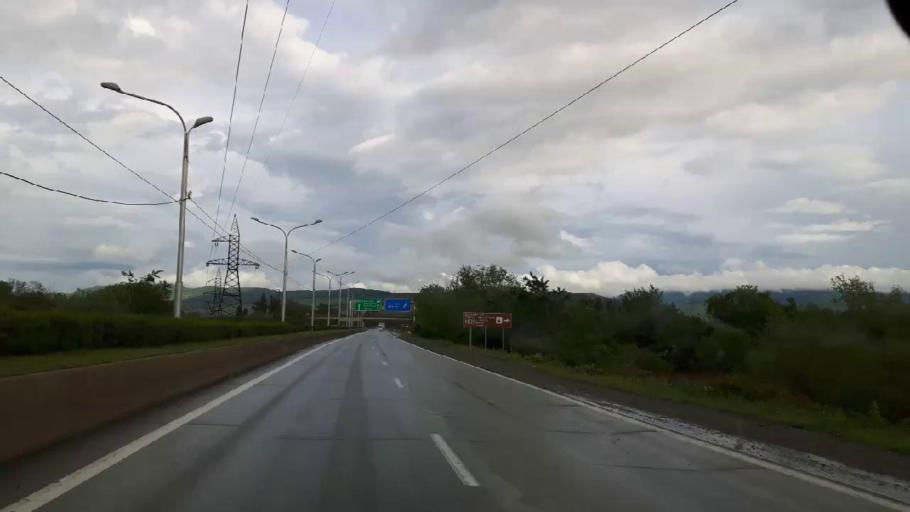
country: GE
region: Shida Kartli
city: Kaspi
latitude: 41.9150
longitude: 44.5567
